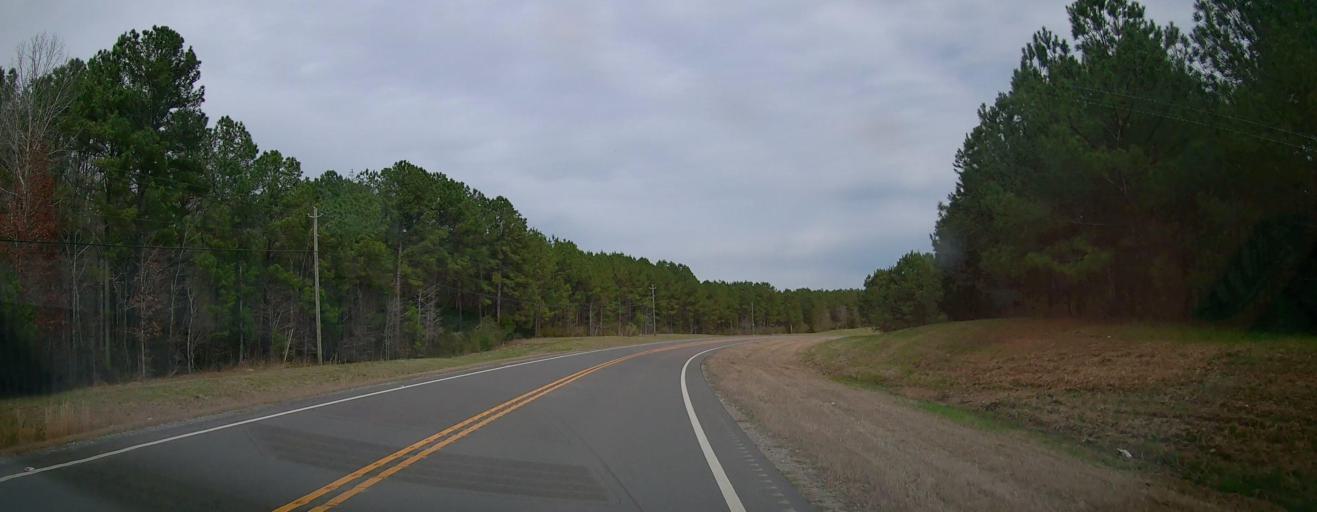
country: US
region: Alabama
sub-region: Walker County
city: Carbon Hill
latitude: 33.8670
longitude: -87.4154
